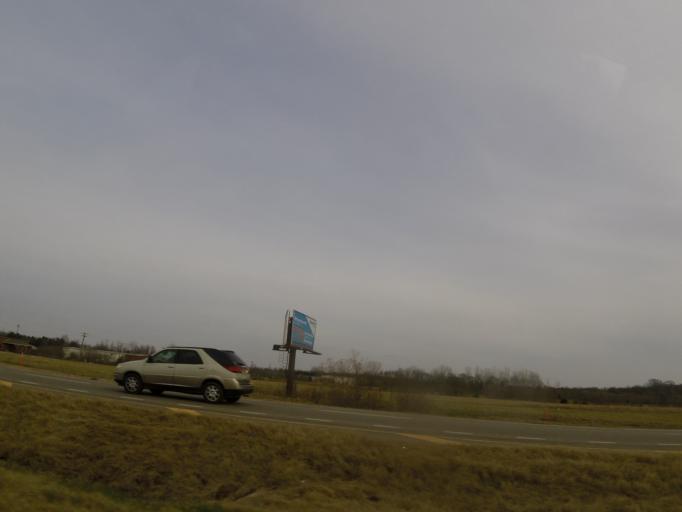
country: US
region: Alabama
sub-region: Montgomery County
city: Montgomery
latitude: 32.3074
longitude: -86.2161
